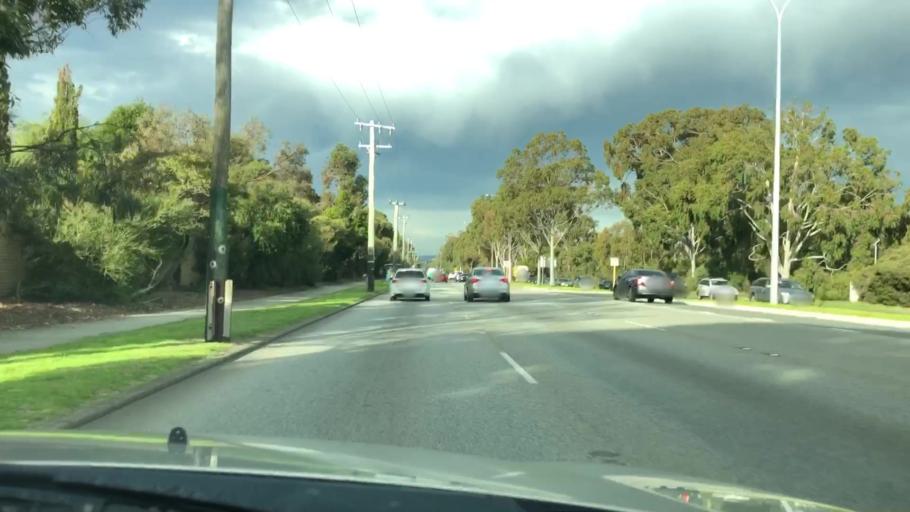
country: AU
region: Western Australia
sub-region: Melville
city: Winthrop
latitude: -32.0459
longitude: 115.8310
